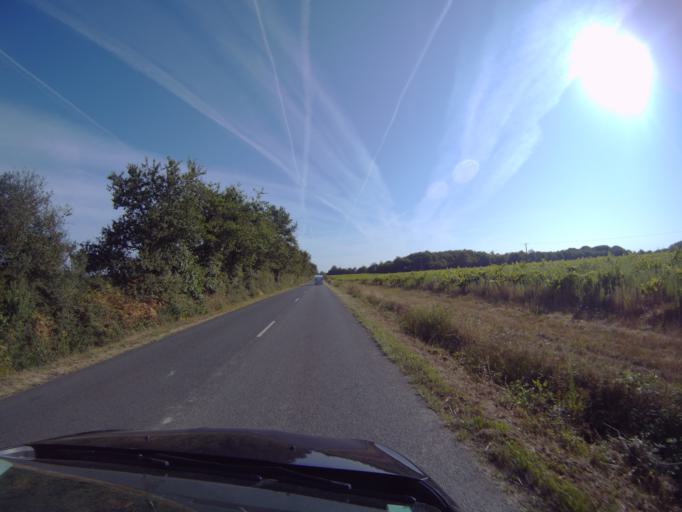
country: FR
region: Pays de la Loire
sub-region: Departement de la Vendee
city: Grosbreuil
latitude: 46.5200
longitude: -1.5566
